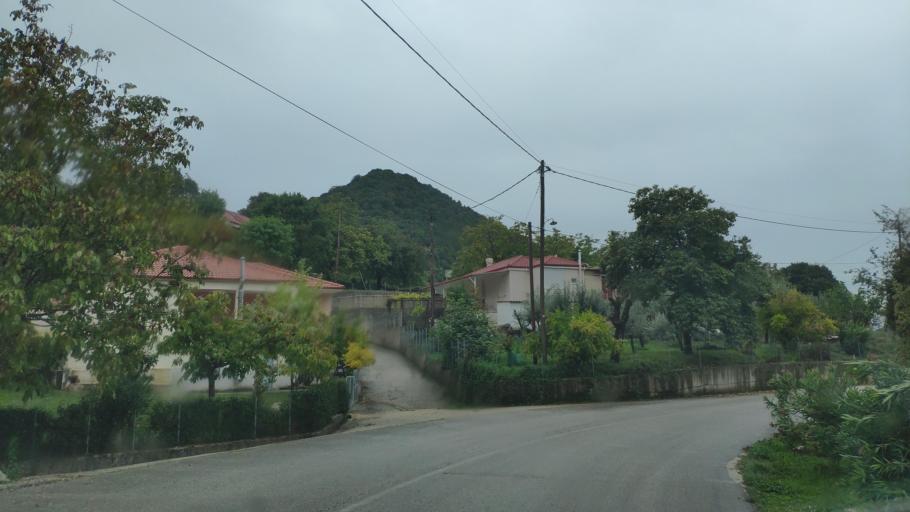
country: GR
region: Epirus
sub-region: Nomos Thesprotias
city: Paramythia
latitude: 39.4168
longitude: 20.6238
